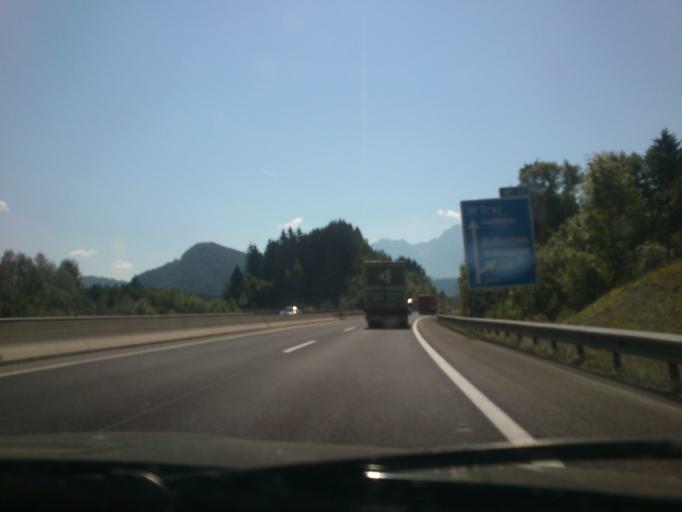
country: AT
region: Upper Austria
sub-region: Politischer Bezirk Kirchdorf an der Krems
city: Rossleithen
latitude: 47.7379
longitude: 14.2877
